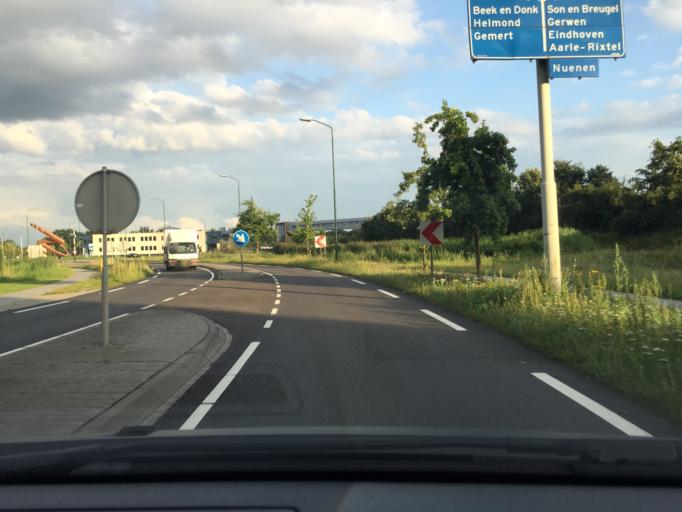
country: NL
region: North Brabant
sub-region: Gemeente Laarbeek
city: Aarle-Rixtel
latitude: 51.5190
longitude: 5.6046
